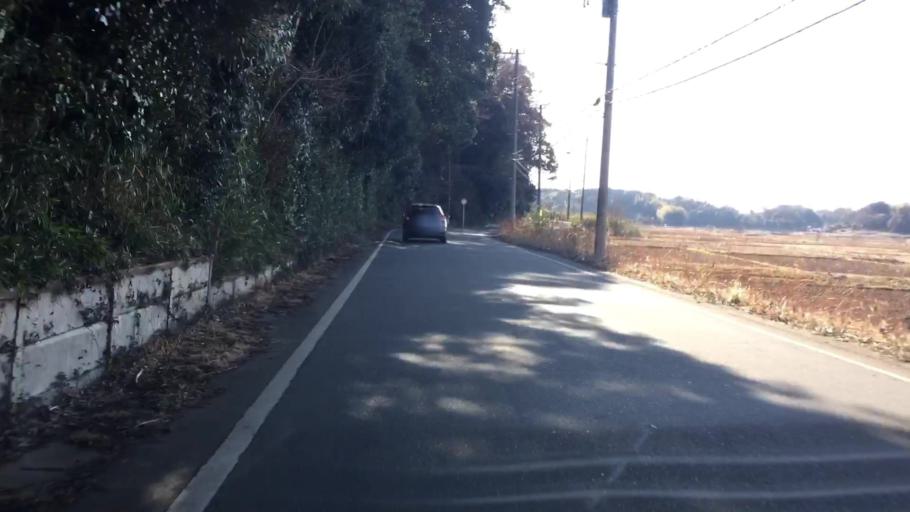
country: JP
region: Chiba
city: Shiroi
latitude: 35.8237
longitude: 140.1223
